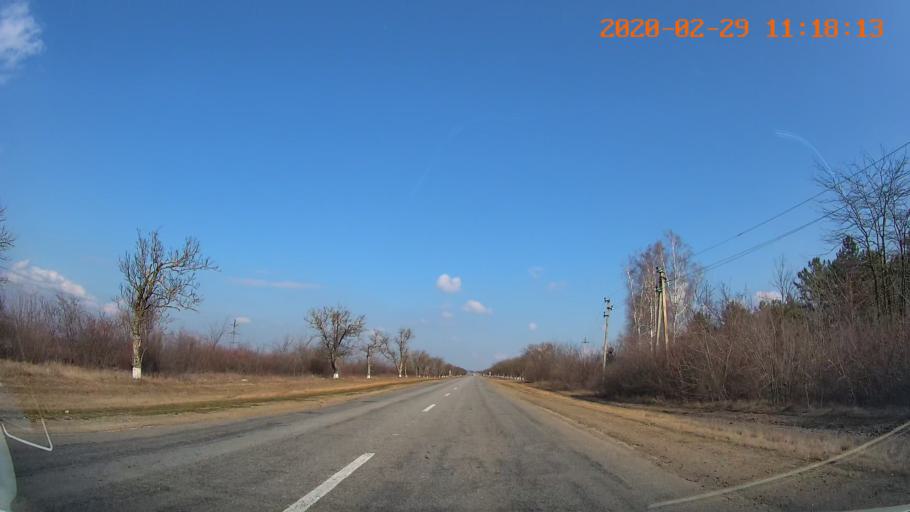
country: MD
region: Telenesti
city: Cocieri
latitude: 47.3320
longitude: 29.1722
